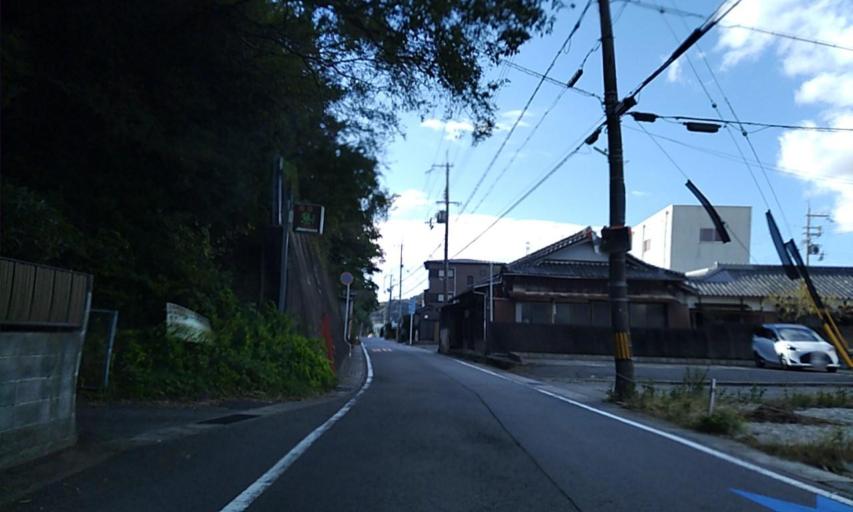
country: JP
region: Wakayama
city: Minato
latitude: 34.2800
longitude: 135.0753
